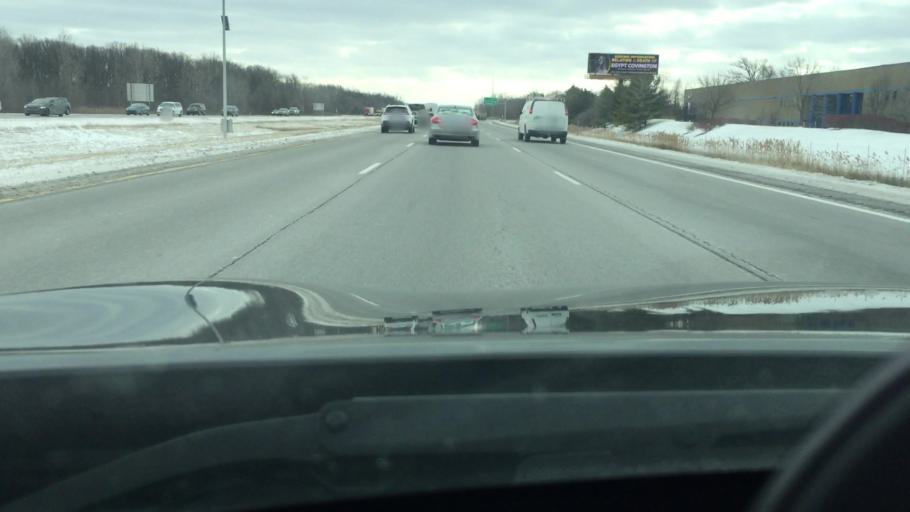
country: US
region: Michigan
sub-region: Wayne County
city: Romulus
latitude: 42.2577
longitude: -83.4407
